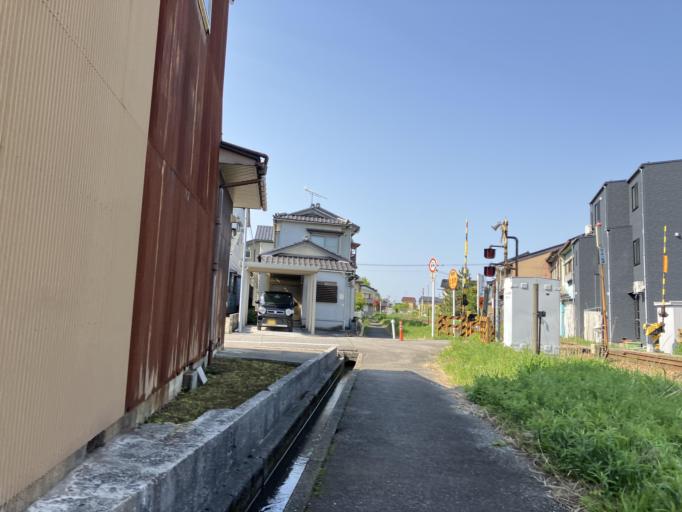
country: JP
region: Toyama
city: Takaoka
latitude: 36.7452
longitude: 137.0254
